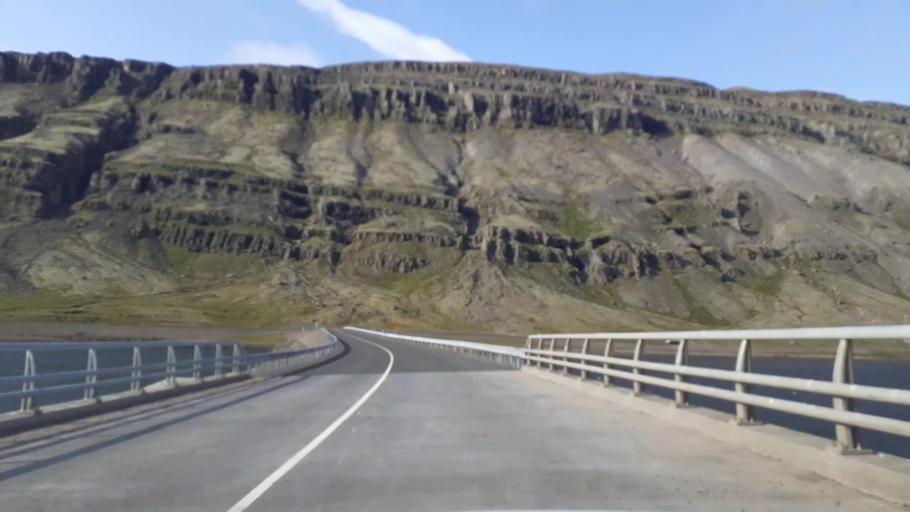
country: IS
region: East
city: Reydarfjoerdur
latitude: 64.7884
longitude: -14.4895
